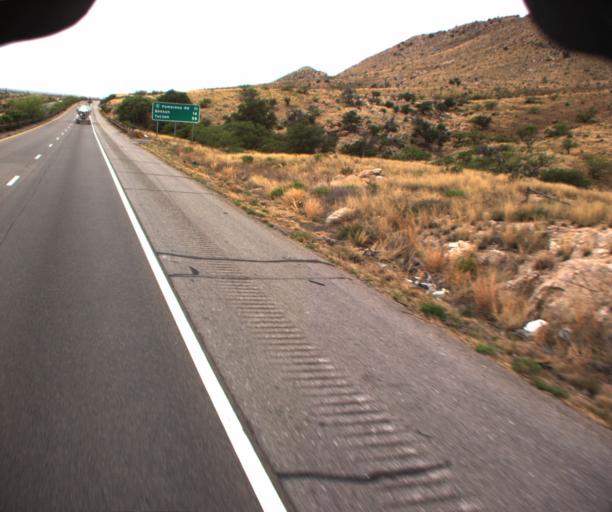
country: US
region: Arizona
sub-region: Cochise County
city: Saint David
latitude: 32.0301
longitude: -110.1053
